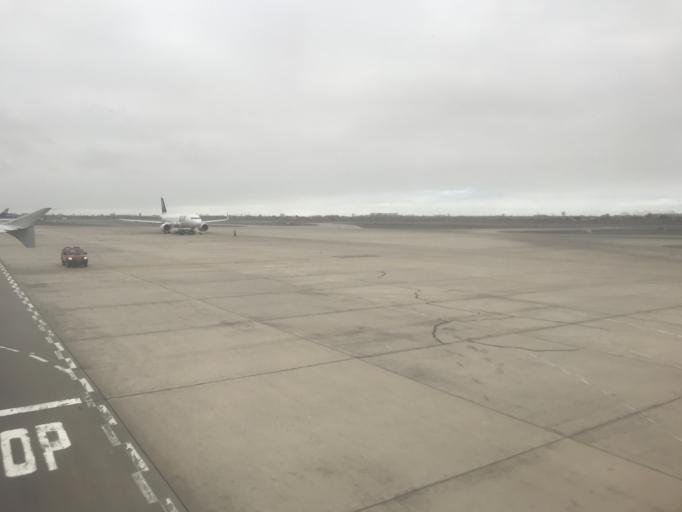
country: PE
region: Callao
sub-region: Callao
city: Callao
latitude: -12.0225
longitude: -77.1106
